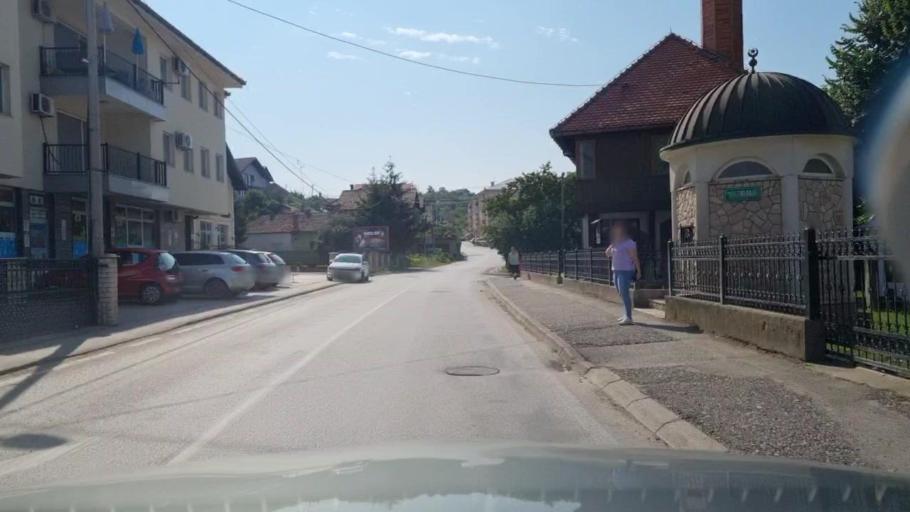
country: BA
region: Federation of Bosnia and Herzegovina
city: Gradacac
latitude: 44.8768
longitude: 18.4328
